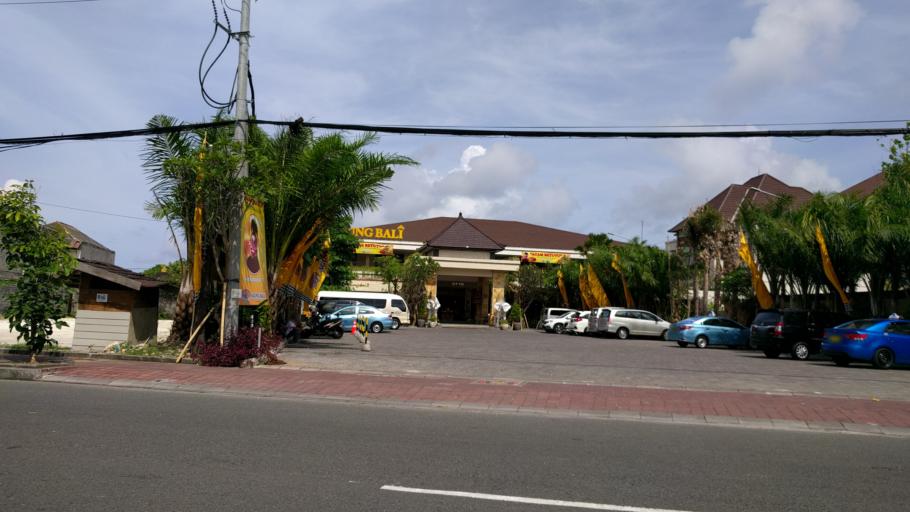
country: ID
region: Bali
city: Kuta
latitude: -8.7009
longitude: 115.1771
